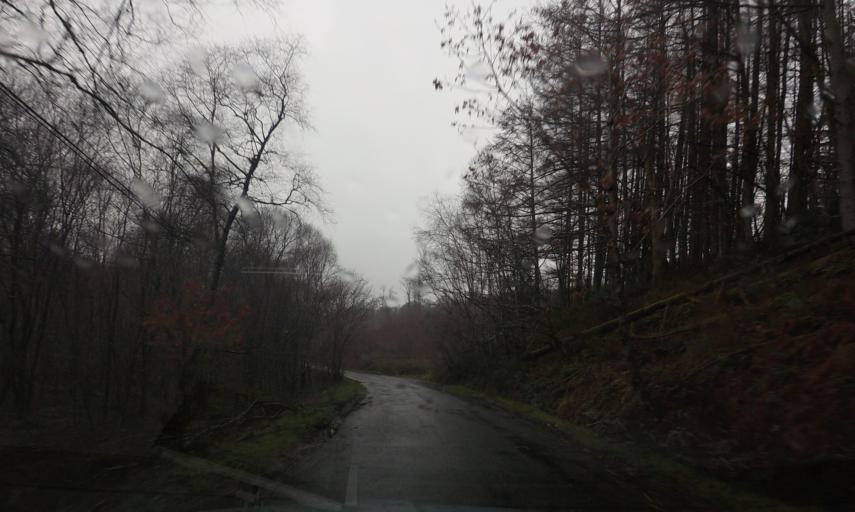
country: GB
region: Scotland
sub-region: West Dunbartonshire
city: Balloch
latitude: 56.1315
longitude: -4.6103
